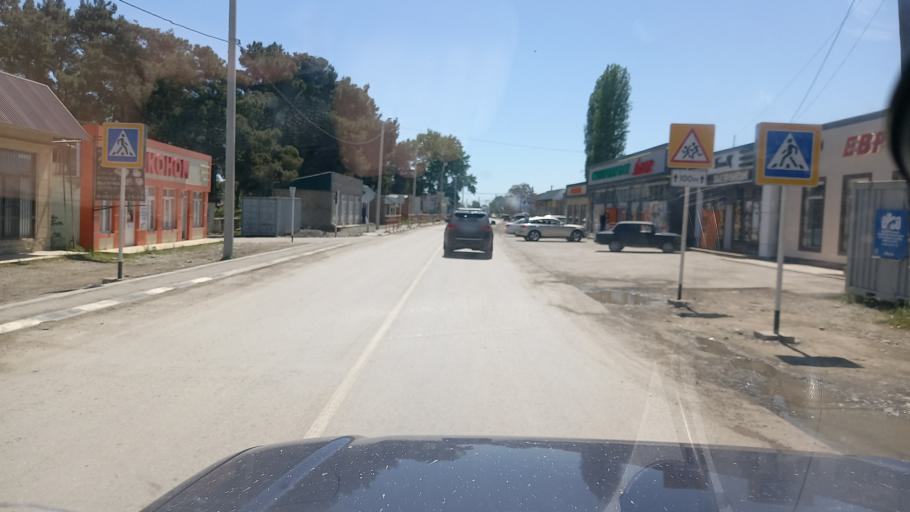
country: RU
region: Dagestan
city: Samur
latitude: 41.8154
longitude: 48.5077
